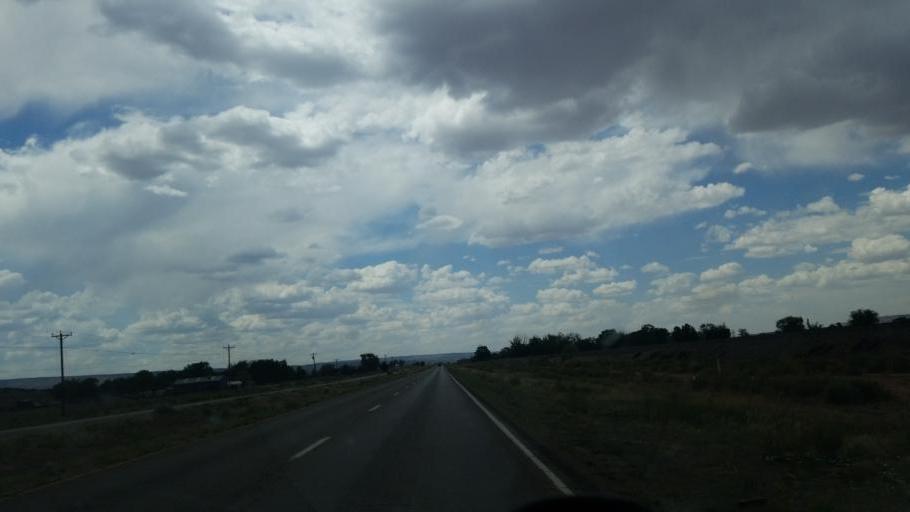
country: US
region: New Mexico
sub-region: Cibola County
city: Milan
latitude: 35.2296
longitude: -107.9277
